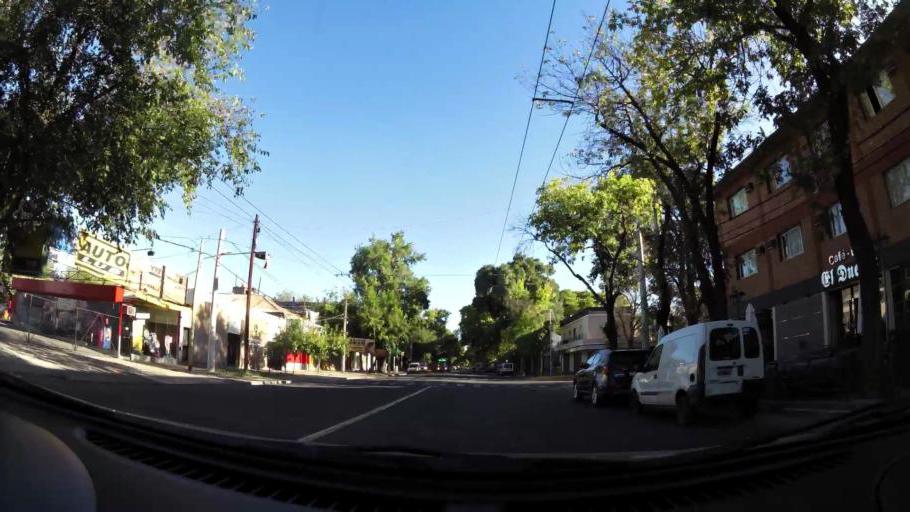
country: AR
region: Mendoza
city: Las Heras
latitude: -32.8698
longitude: -68.8339
